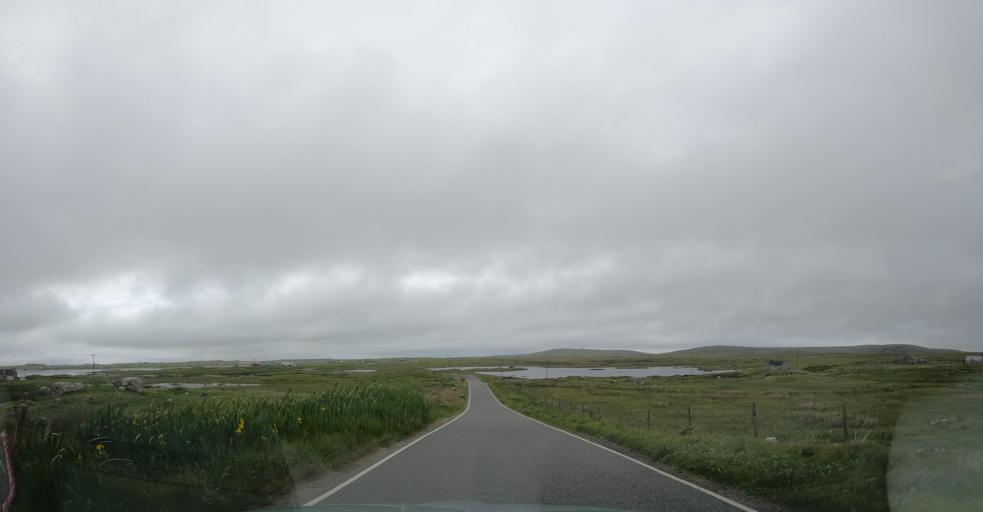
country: GB
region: Scotland
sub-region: Eilean Siar
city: Isle of North Uist
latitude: 57.5777
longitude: -7.4078
